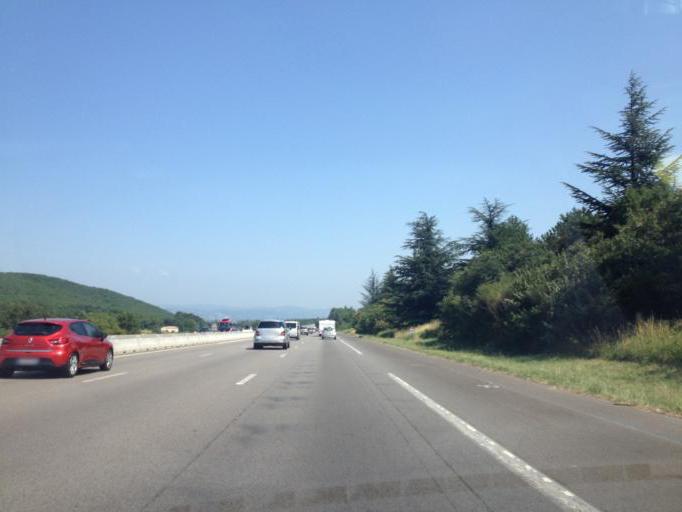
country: FR
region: Rhone-Alpes
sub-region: Departement de la Drome
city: Savasse
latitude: 44.6276
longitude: 4.7929
